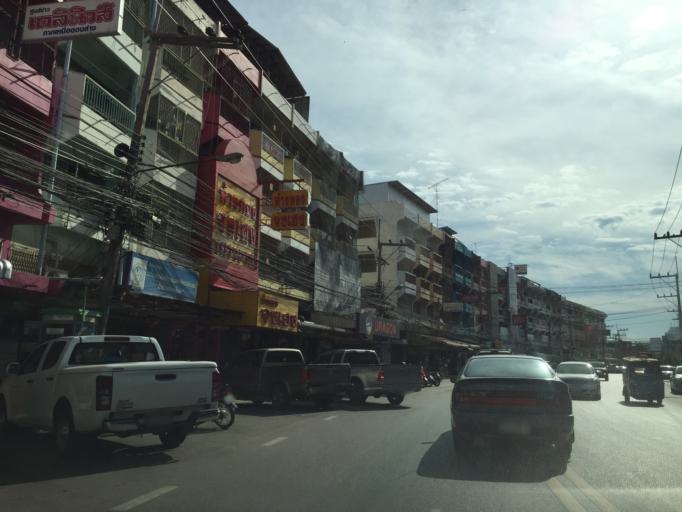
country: TH
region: Phitsanulok
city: Phitsanulok
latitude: 16.8204
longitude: 100.2695
